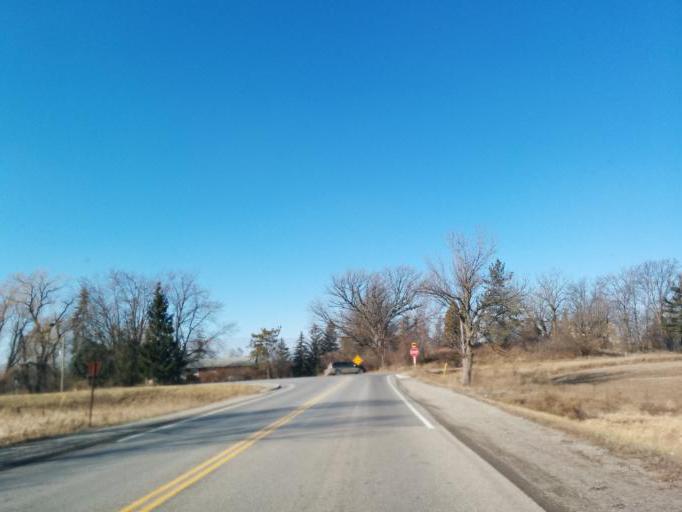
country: CA
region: Ontario
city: Brantford
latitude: 43.0422
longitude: -80.2715
